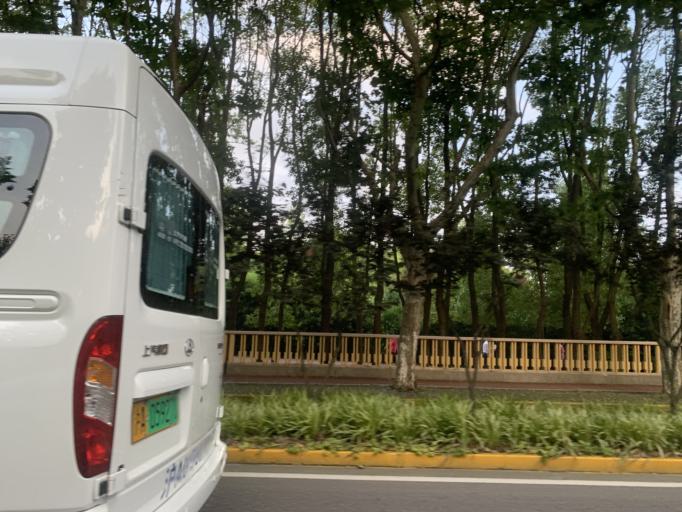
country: CN
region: Shanghai Shi
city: Huamu
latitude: 31.2186
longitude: 121.5404
